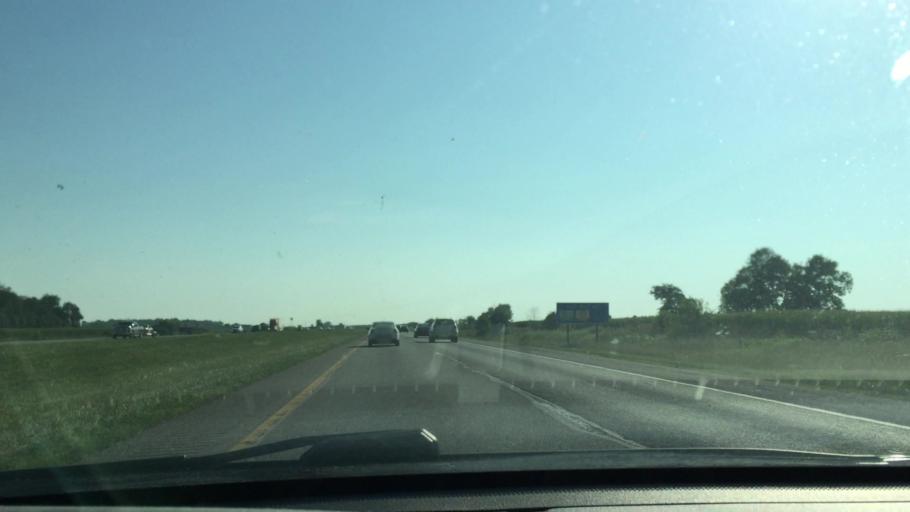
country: US
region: Ohio
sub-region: Clinton County
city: Wilmington
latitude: 39.4920
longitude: -83.9243
